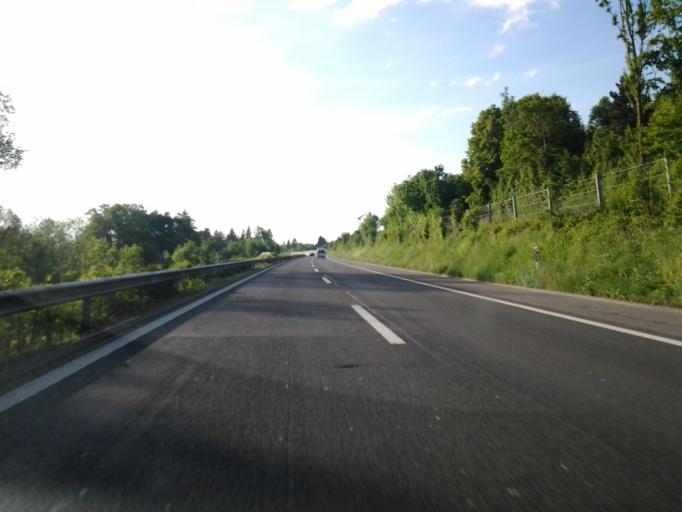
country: CH
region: Lucerne
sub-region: Sursee District
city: Schenkon
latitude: 47.1645
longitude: 8.1453
